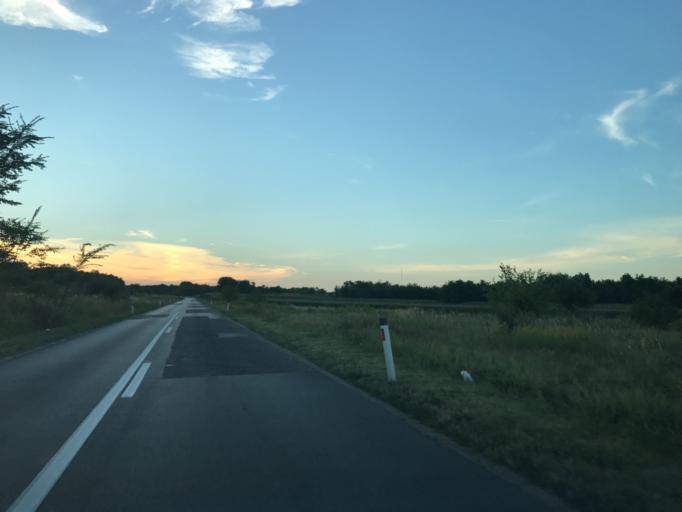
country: RS
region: Central Serbia
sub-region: Branicevski Okrug
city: Golubac
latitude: 44.6830
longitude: 21.5872
